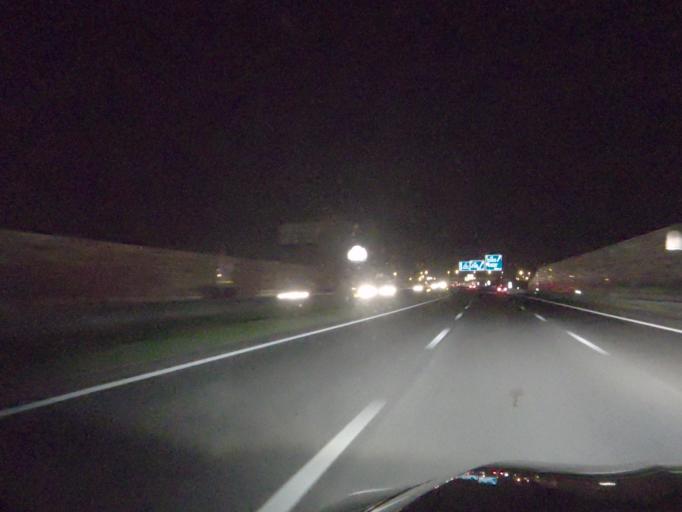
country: PT
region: Lisbon
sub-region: Vila Franca de Xira
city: Castanheira do Ribatejo
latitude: 38.9979
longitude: -8.9676
